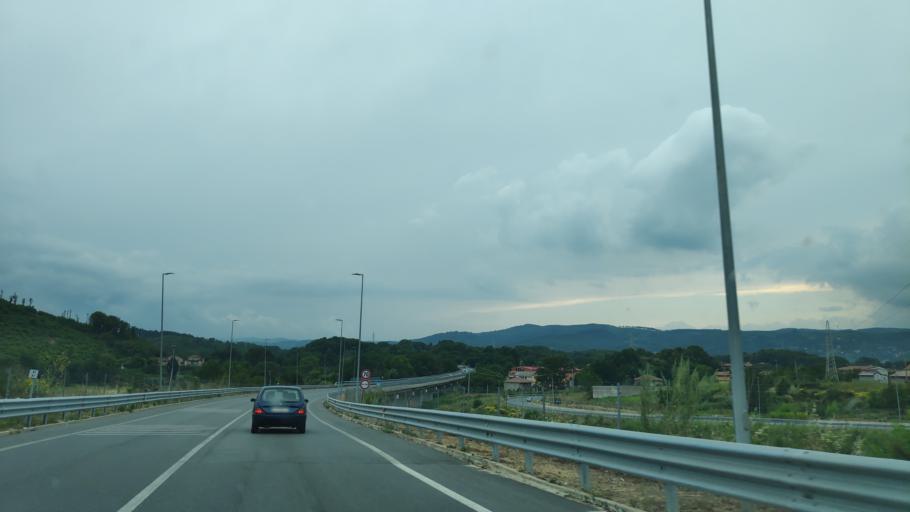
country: IT
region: Calabria
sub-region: Provincia di Catanzaro
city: Chiaravalle Centrale
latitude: 38.6740
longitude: 16.4121
